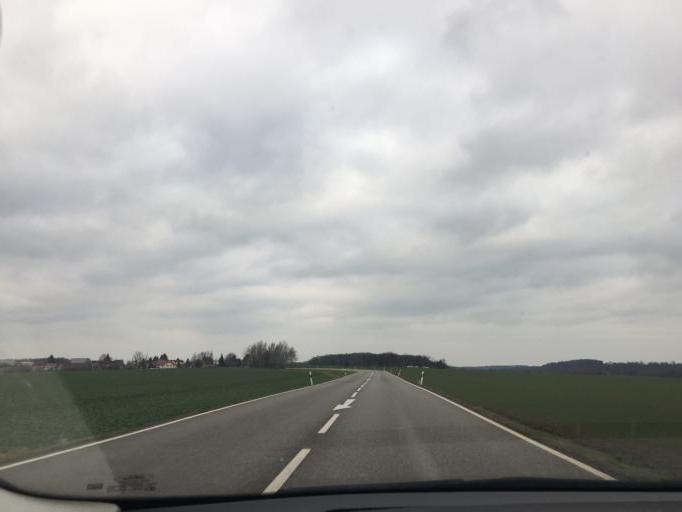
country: DE
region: Thuringia
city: Langenleuba-Niederhain
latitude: 50.9909
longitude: 12.6047
